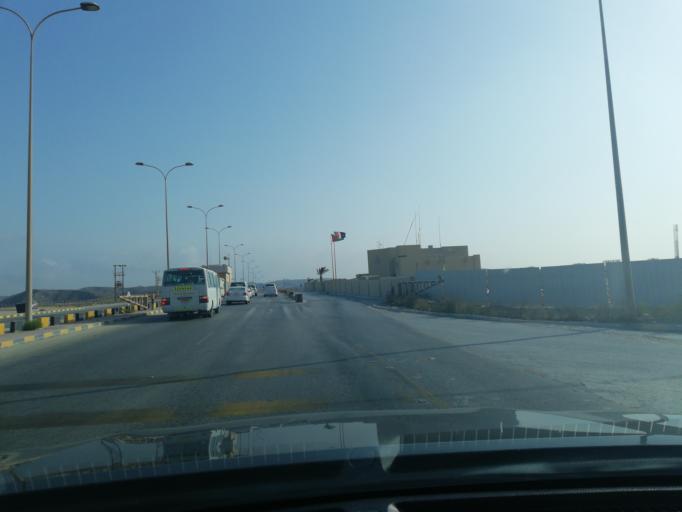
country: OM
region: Zufar
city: Salalah
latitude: 17.2794
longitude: 54.0864
